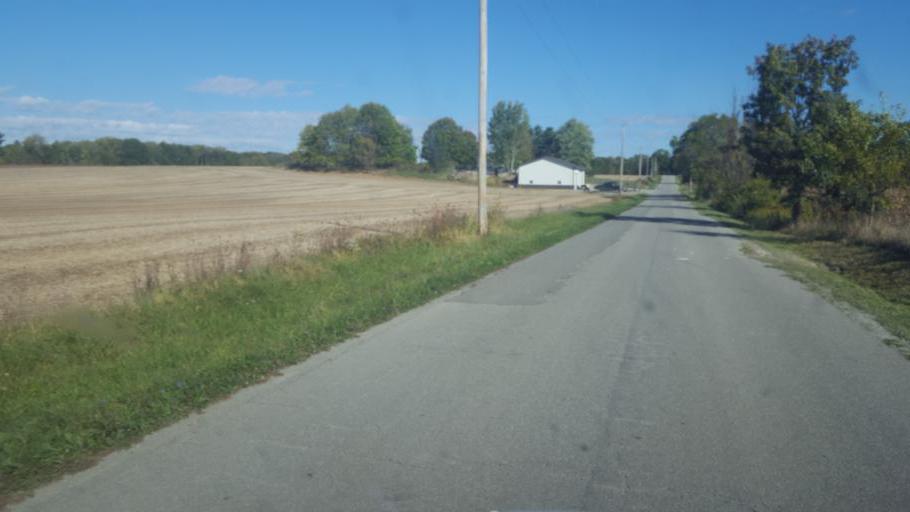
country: US
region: Ohio
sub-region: Wyandot County
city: Upper Sandusky
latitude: 40.7763
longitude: -83.2172
